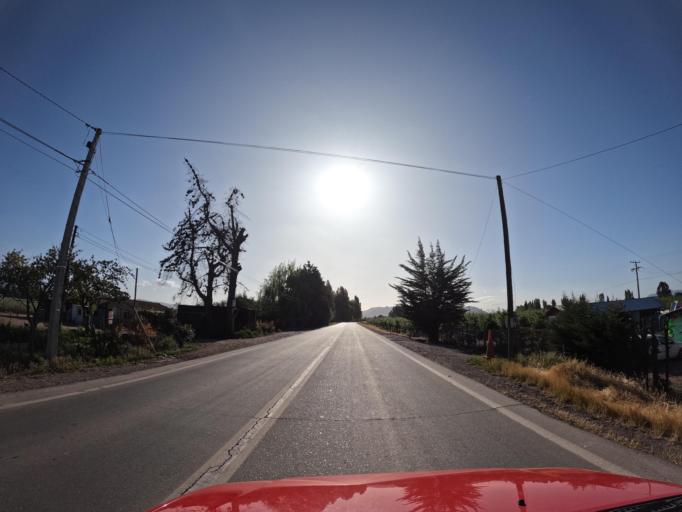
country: CL
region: O'Higgins
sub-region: Provincia de Colchagua
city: Santa Cruz
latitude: -34.7403
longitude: -71.2516
